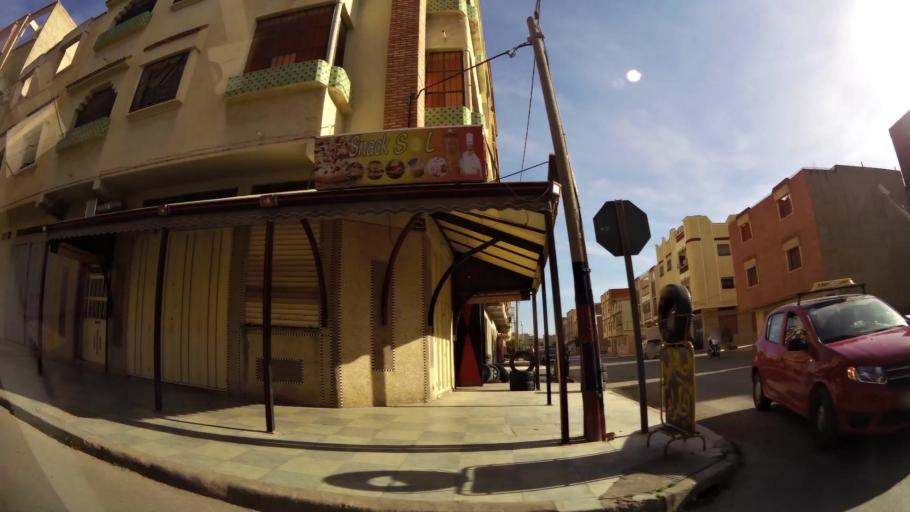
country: MA
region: Oriental
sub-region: Oujda-Angad
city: Oujda
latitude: 34.6703
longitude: -1.8969
